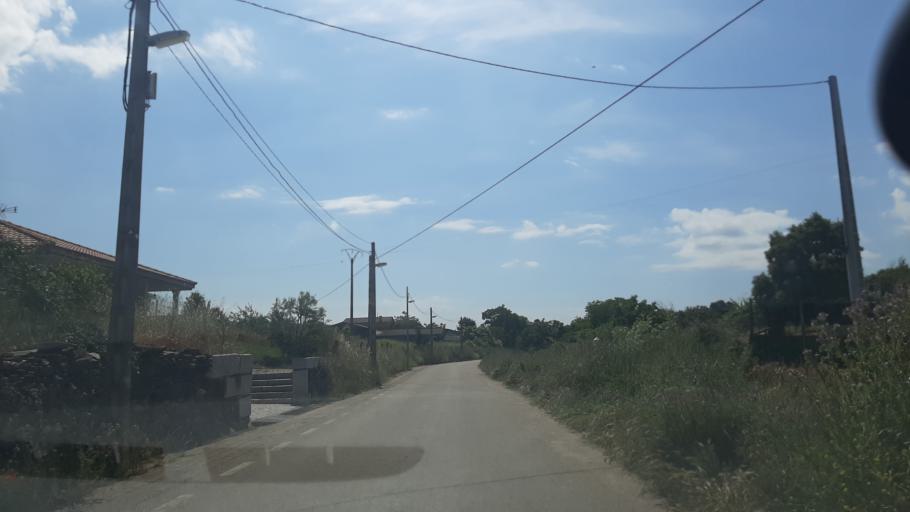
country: ES
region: Castille and Leon
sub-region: Provincia de Salamanca
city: Gallegos de Arganan
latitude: 40.6489
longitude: -6.7563
